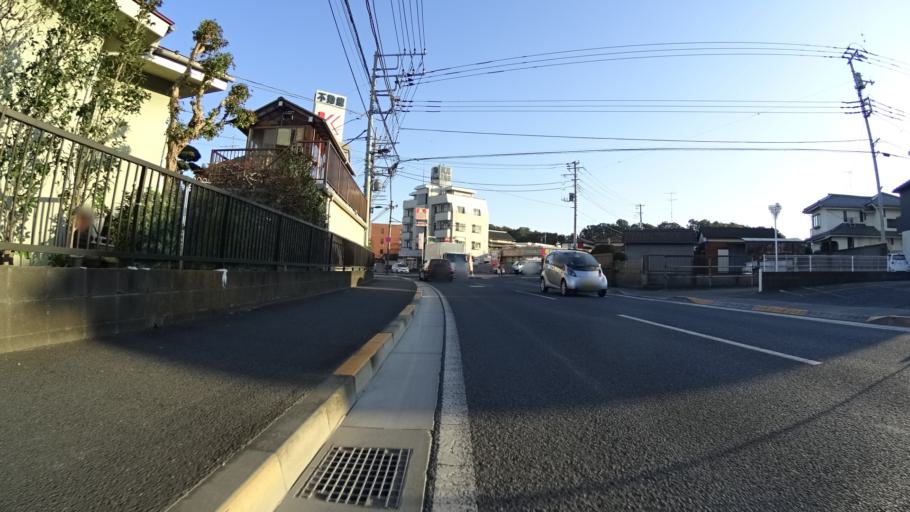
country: JP
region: Tokyo
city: Hachioji
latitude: 35.6664
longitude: 139.3029
